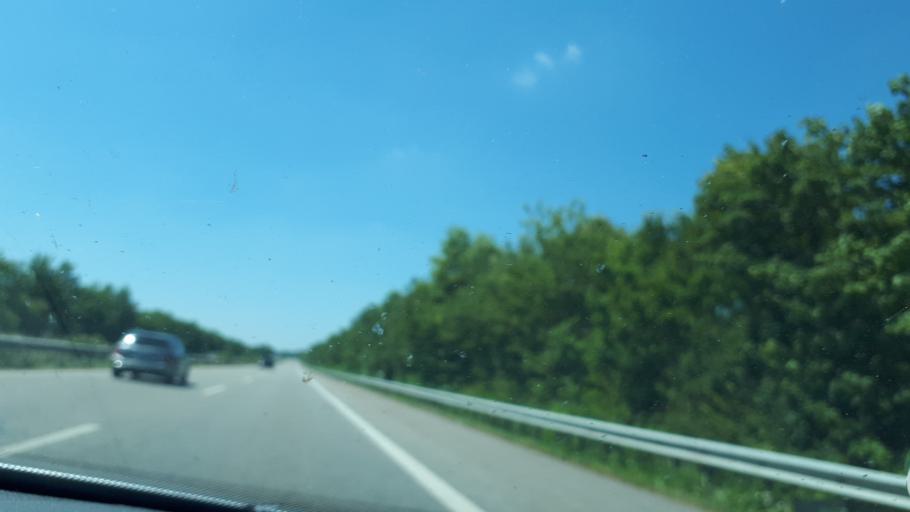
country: DE
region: Rheinland-Pfalz
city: Einig
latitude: 50.2996
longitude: 7.2758
